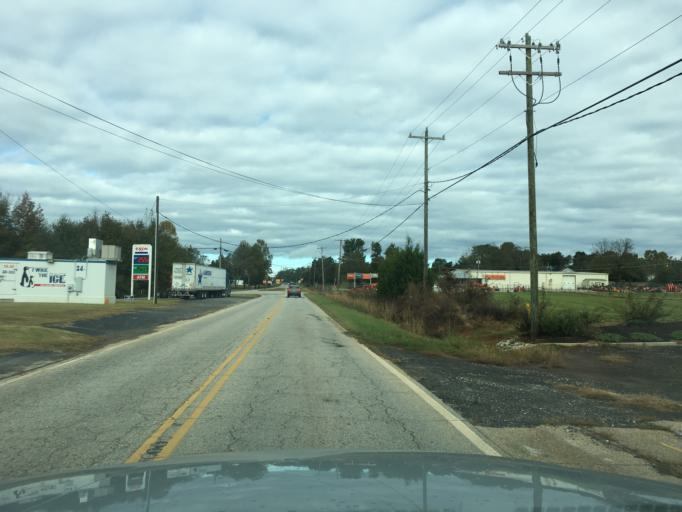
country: US
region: South Carolina
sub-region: Greenville County
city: Greer
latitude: 34.9915
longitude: -82.2446
